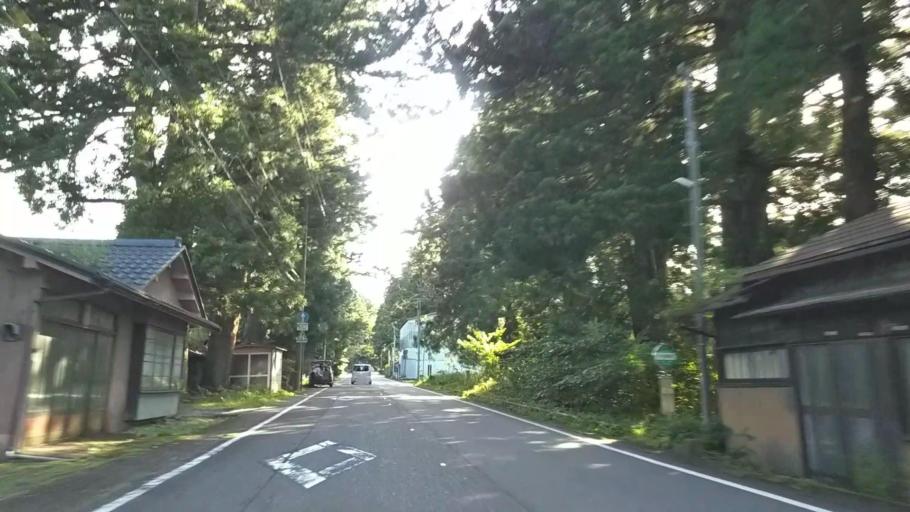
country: JP
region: Tochigi
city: Imaichi
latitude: 36.7354
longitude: 139.6952
